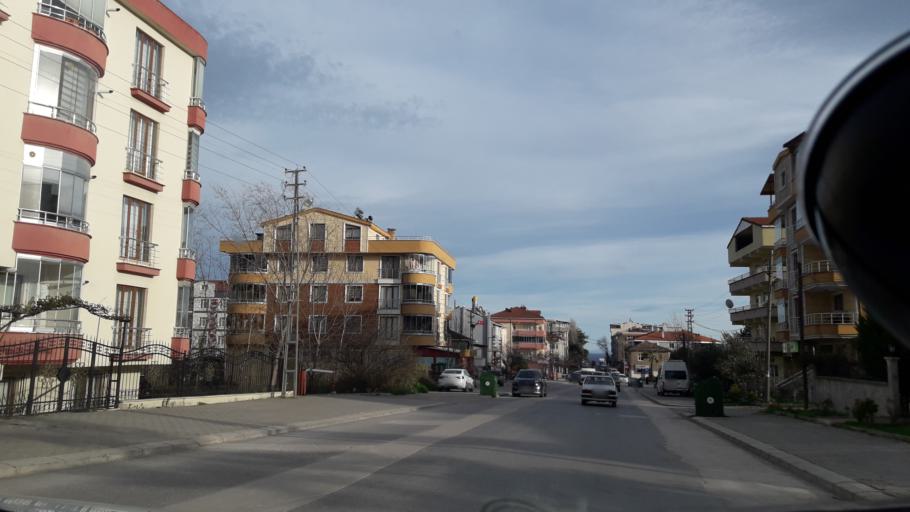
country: TR
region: Sinop
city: Gerze
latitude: 41.8067
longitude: 35.1885
